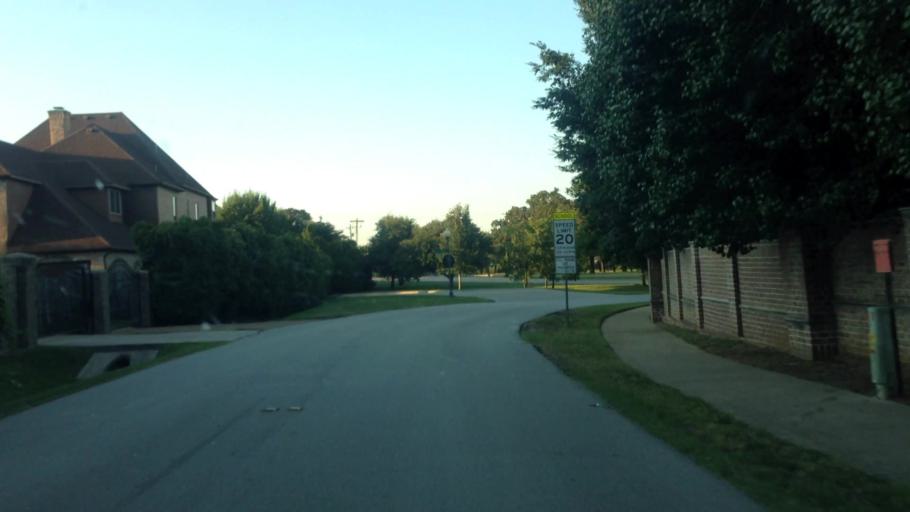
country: US
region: Texas
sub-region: Tarrant County
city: Southlake
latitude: 32.9285
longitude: -97.1283
